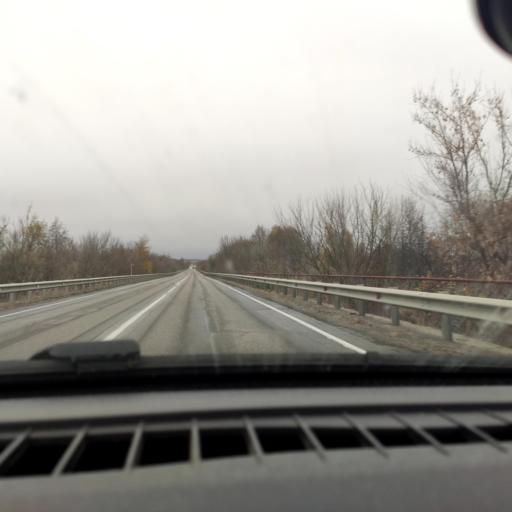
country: RU
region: Voronezj
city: Ostrogozhsk
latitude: 51.0325
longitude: 38.9857
